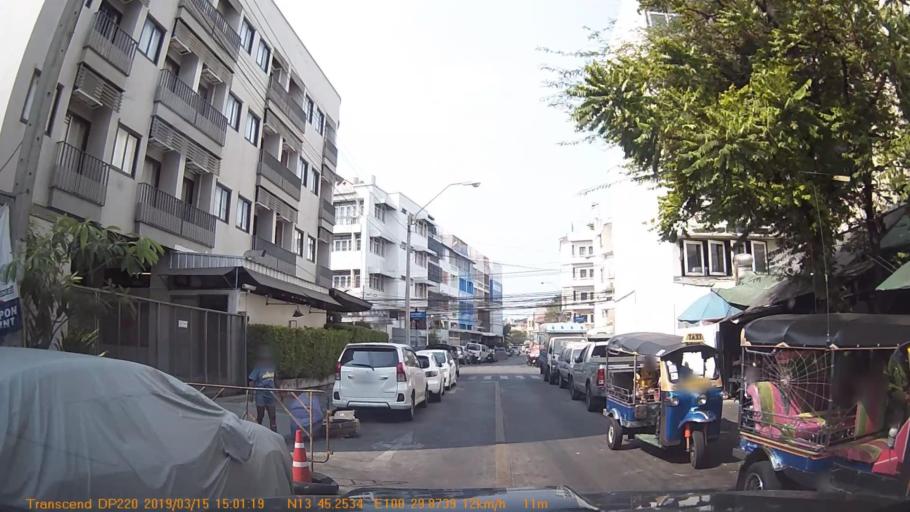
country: TH
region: Bangkok
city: Bangkok
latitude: 13.7543
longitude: 100.4979
